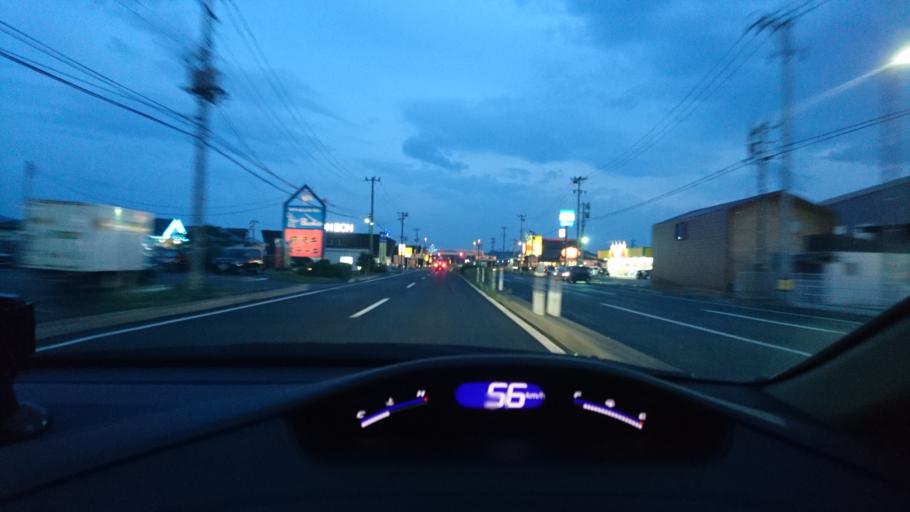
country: JP
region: Iwate
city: Mizusawa
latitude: 39.0481
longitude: 141.1310
